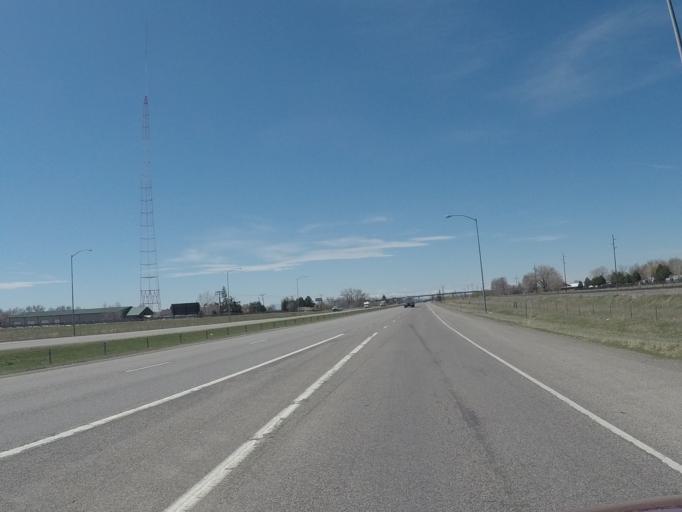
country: US
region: Montana
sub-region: Yellowstone County
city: Billings
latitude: 45.7309
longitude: -108.6083
